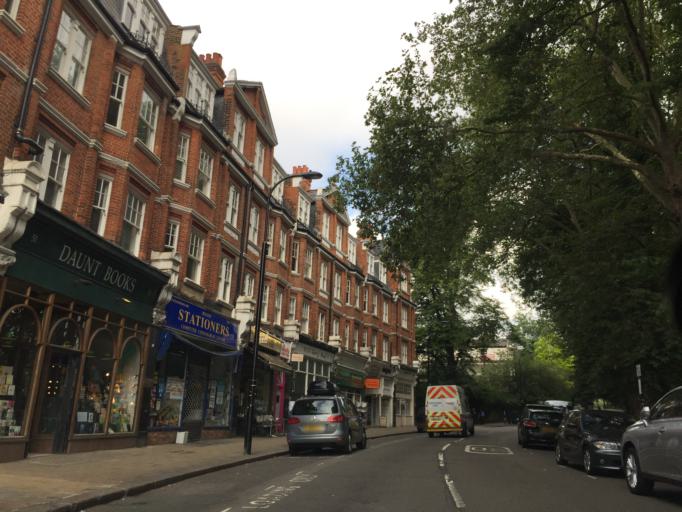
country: GB
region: England
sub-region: Greater London
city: Belsize Park
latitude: 51.5555
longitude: -0.1664
